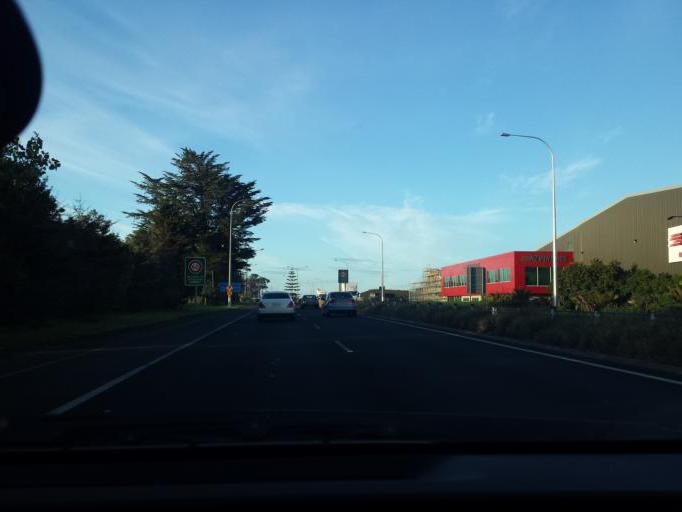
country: NZ
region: Auckland
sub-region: Auckland
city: Mangere
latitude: -36.9886
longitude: 174.7859
